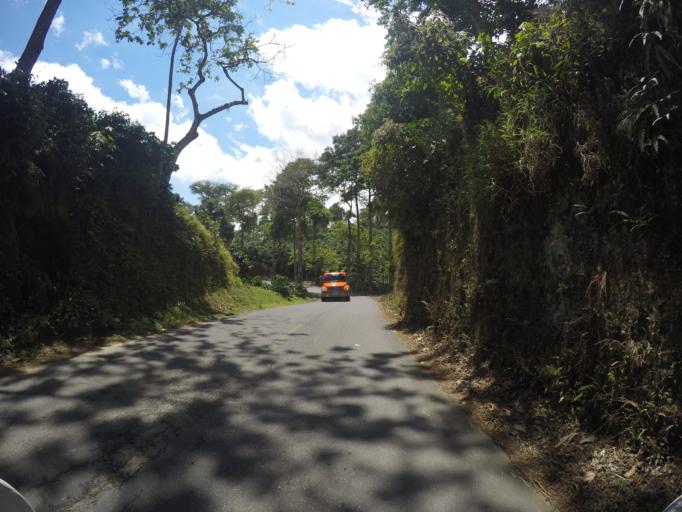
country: CO
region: Quindio
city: Quimbaya
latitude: 4.6299
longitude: -75.7217
